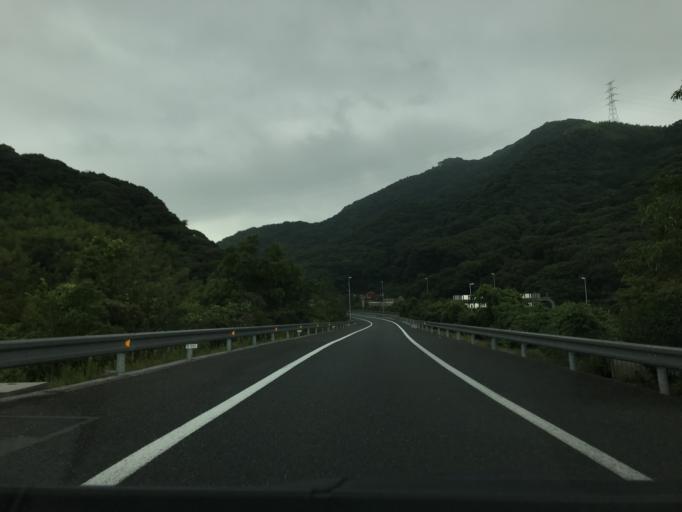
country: JP
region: Fukuoka
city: Kitakyushu
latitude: 33.8154
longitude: 130.8872
